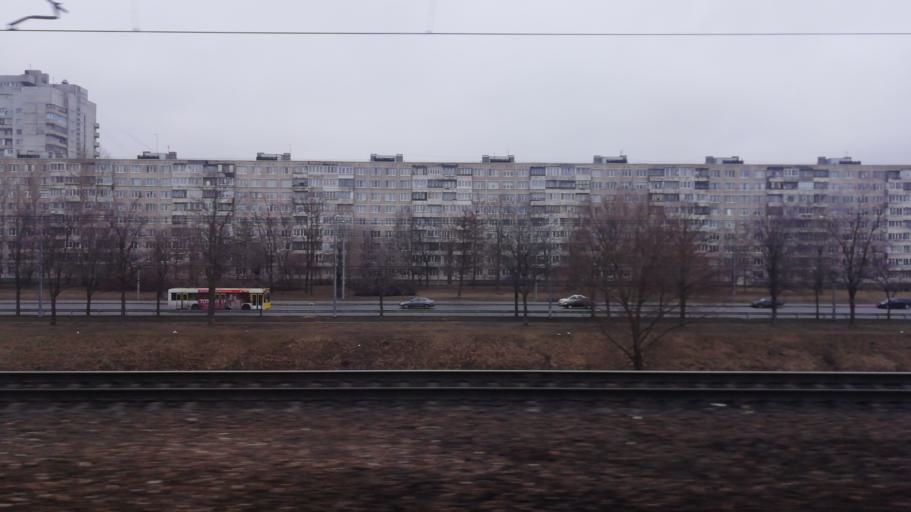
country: RU
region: St.-Petersburg
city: Kupchino
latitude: 59.8680
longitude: 30.3574
